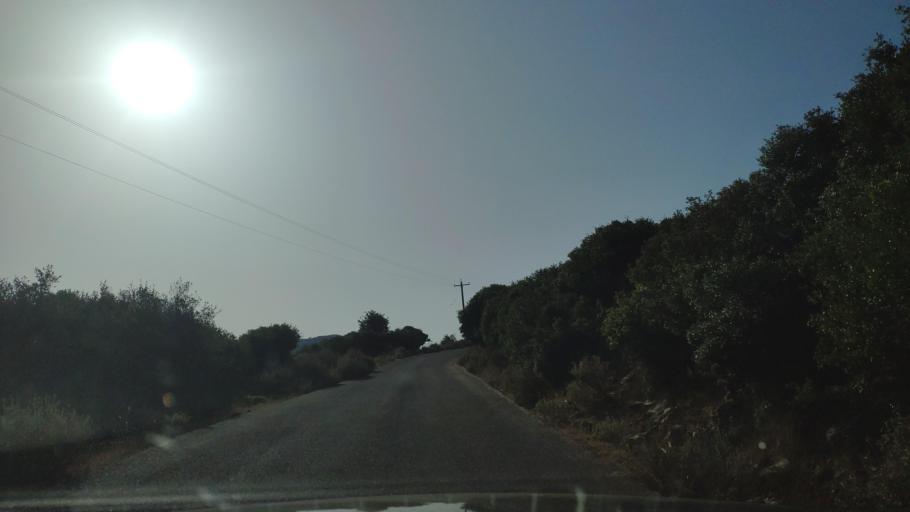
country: GR
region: West Greece
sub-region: Nomos Aitolias kai Akarnanias
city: Monastirakion
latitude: 38.8447
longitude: 20.9725
